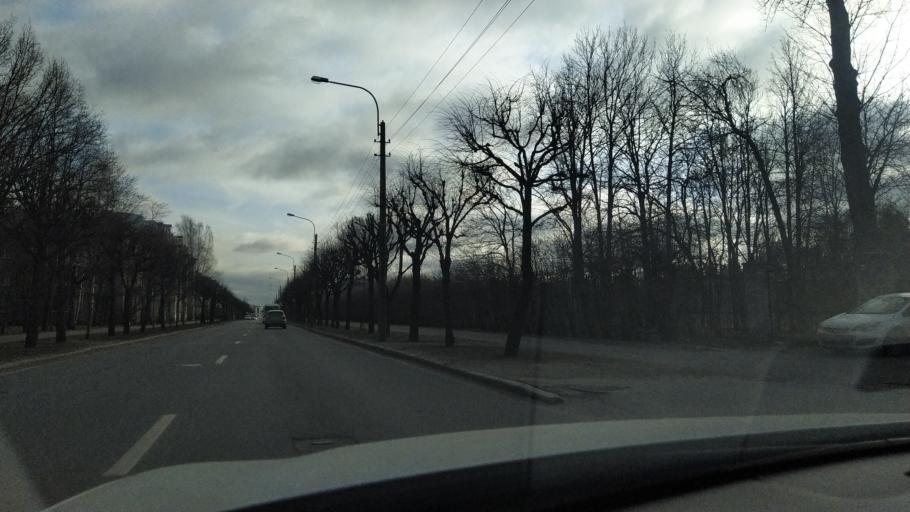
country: RU
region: St.-Petersburg
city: Pushkin
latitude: 59.7261
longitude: 30.4190
